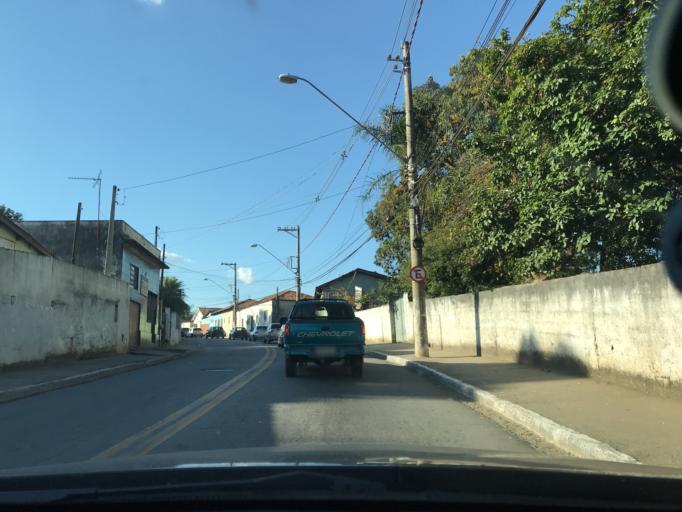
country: BR
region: Sao Paulo
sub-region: Sao Jose Dos Campos
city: Sao Jose dos Campos
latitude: -23.1557
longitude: -45.9016
